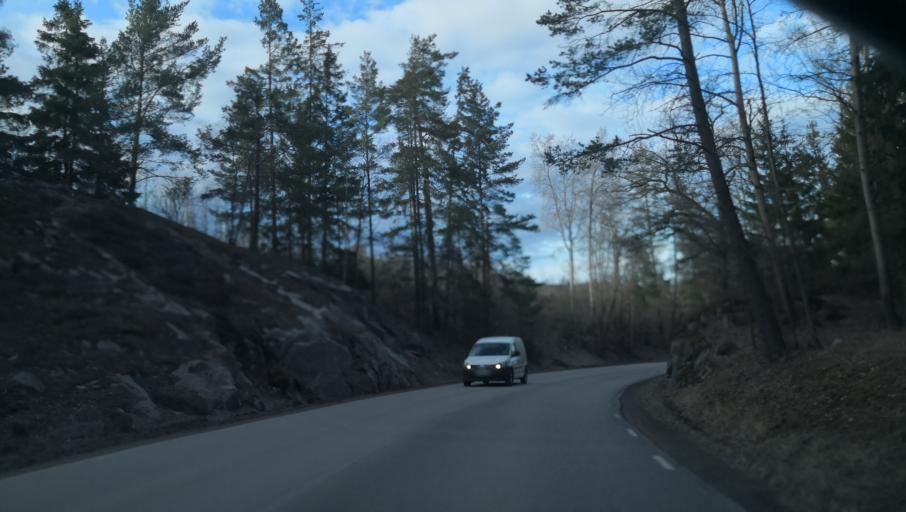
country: SE
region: Stockholm
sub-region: Varmdo Kommun
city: Gustavsberg
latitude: 59.3438
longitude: 18.3555
